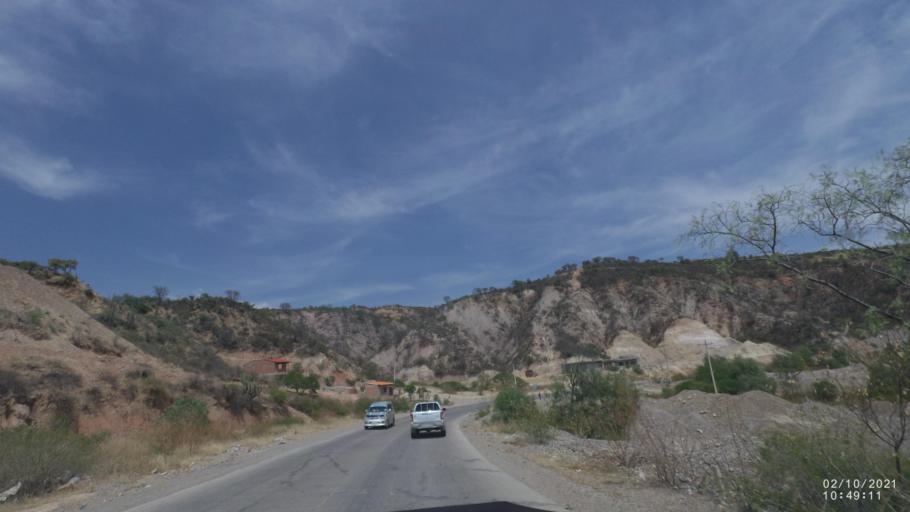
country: BO
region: Cochabamba
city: Sipe Sipe
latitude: -17.5810
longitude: -66.3425
